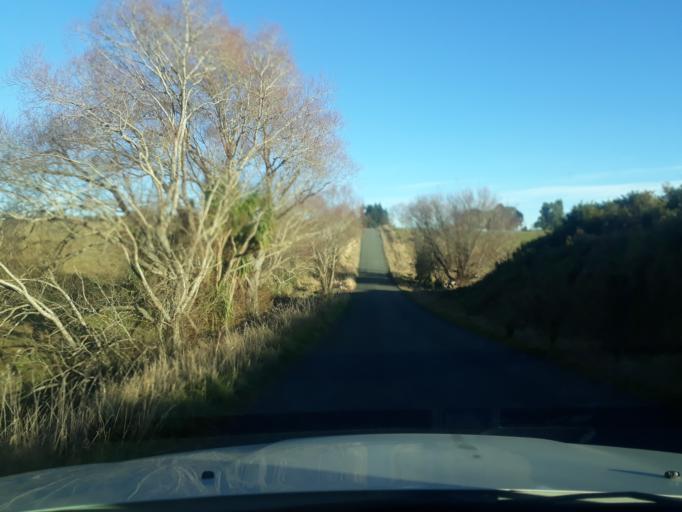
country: NZ
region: Canterbury
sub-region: Timaru District
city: Pleasant Point
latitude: -44.3686
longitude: 171.1403
